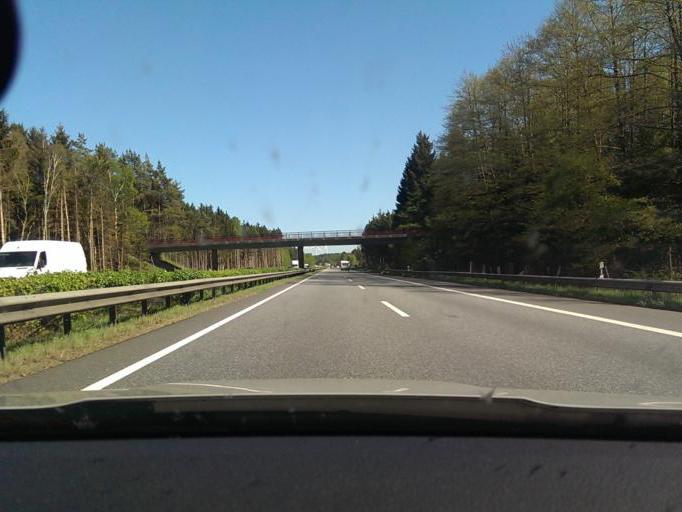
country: DE
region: Lower Saxony
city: Hauslingen
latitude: 52.8966
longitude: 9.4248
